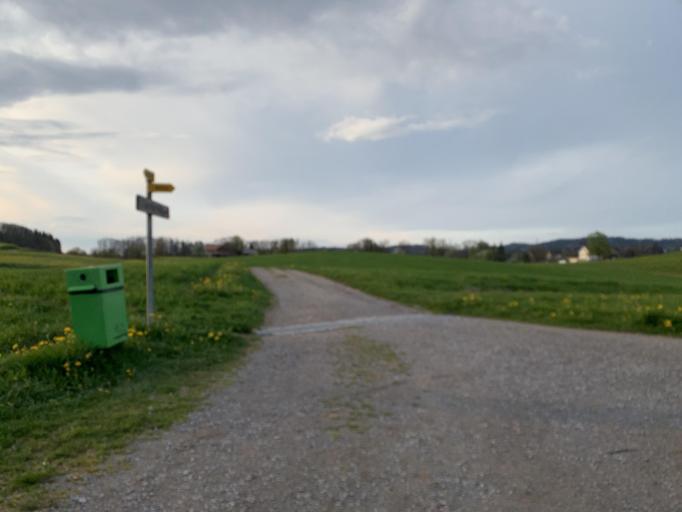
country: CH
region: Zurich
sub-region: Bezirk Hinwil
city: Durnten
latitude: 47.2831
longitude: 8.8493
